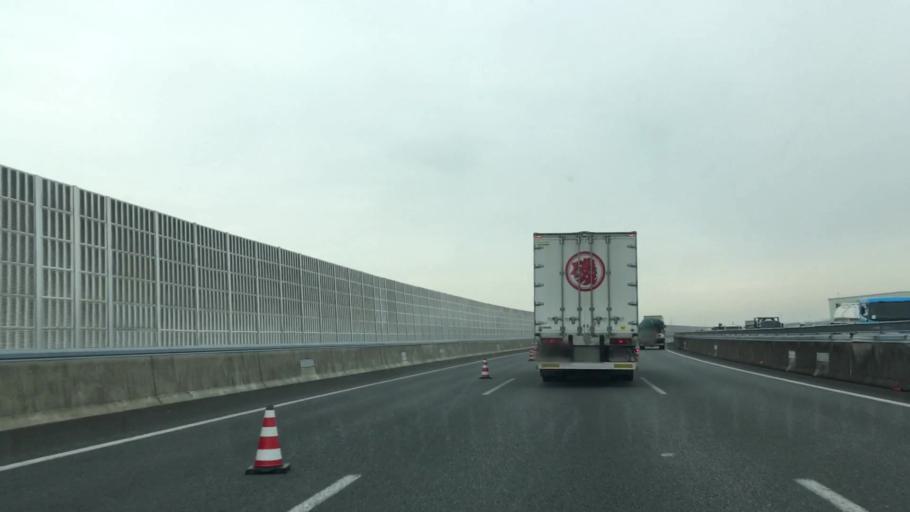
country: JP
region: Aichi
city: Kanie
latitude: 35.0466
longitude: 136.7582
